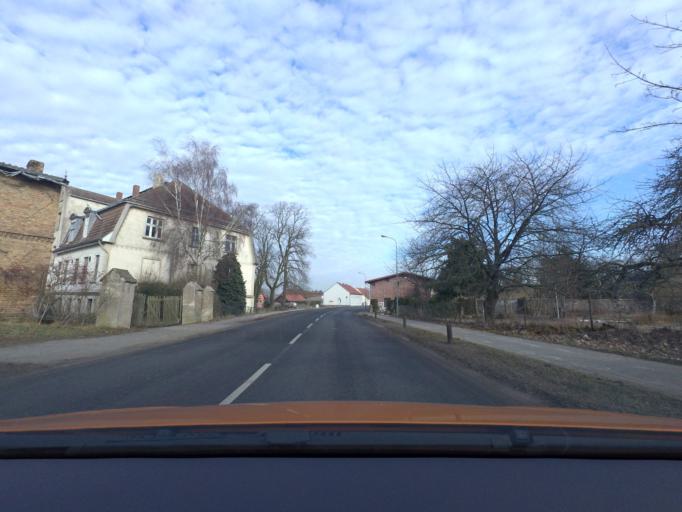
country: DE
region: Brandenburg
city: Gransee
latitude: 52.8948
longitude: 13.1465
